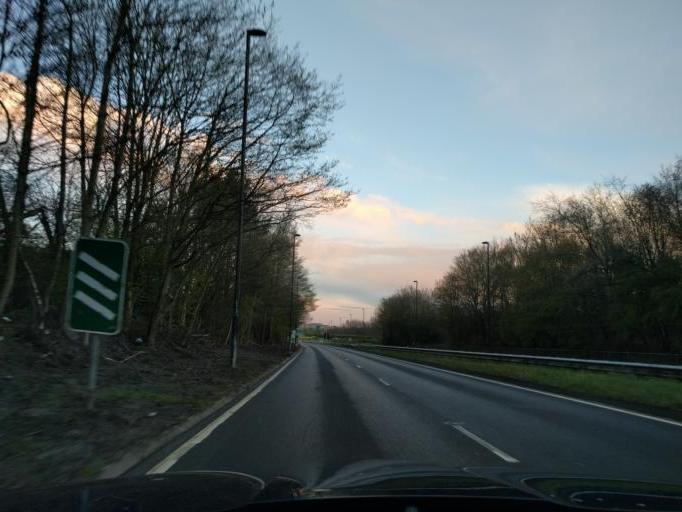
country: GB
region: England
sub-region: Newcastle upon Tyne
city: Gosforth
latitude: 55.0287
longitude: -1.5890
